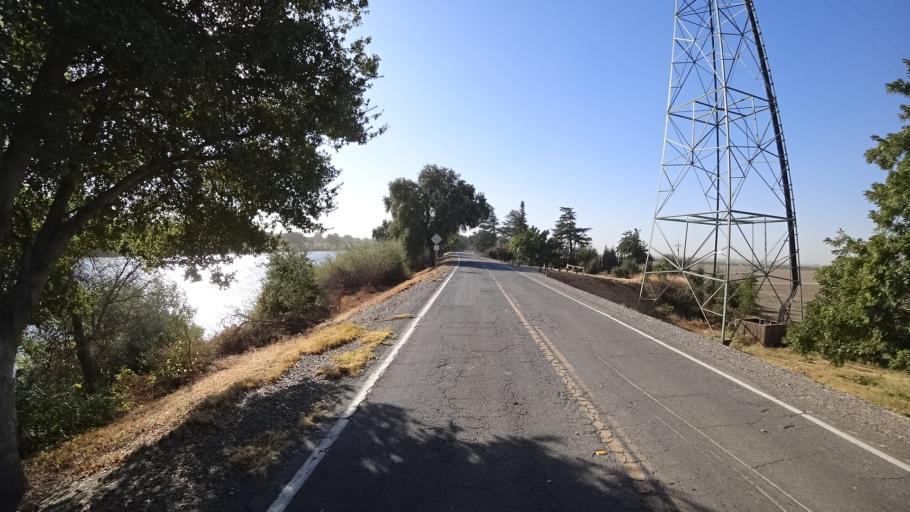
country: US
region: California
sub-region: Sacramento County
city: Parkway
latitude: 38.4669
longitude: -121.5056
